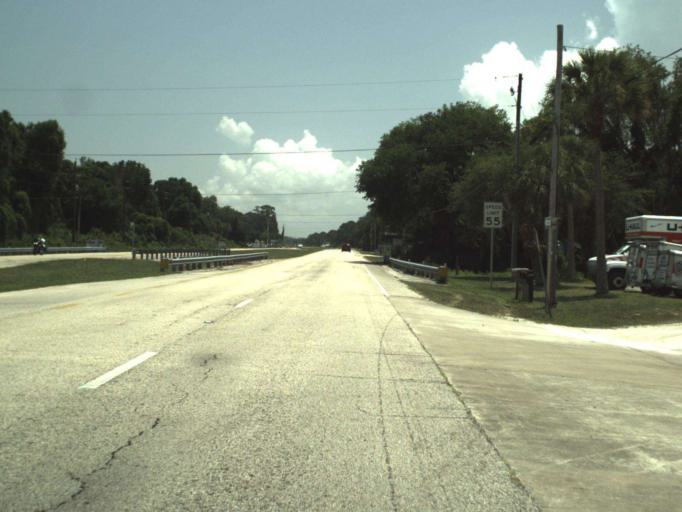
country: US
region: Florida
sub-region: Volusia County
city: Oak Hill
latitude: 28.8972
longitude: -80.8623
